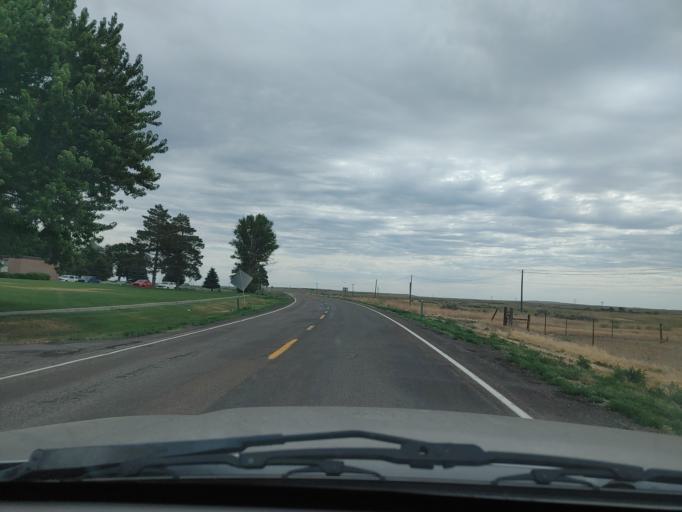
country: US
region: Idaho
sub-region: Lincoln County
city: Shoshone
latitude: 43.0493
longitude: -114.1486
